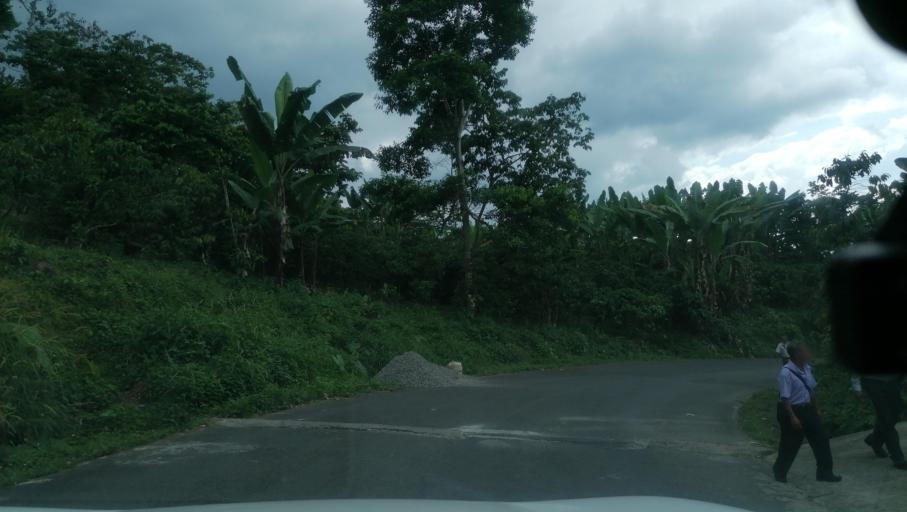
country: MX
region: Chiapas
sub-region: Cacahoatan
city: Benito Juarez
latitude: 15.0830
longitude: -92.1965
